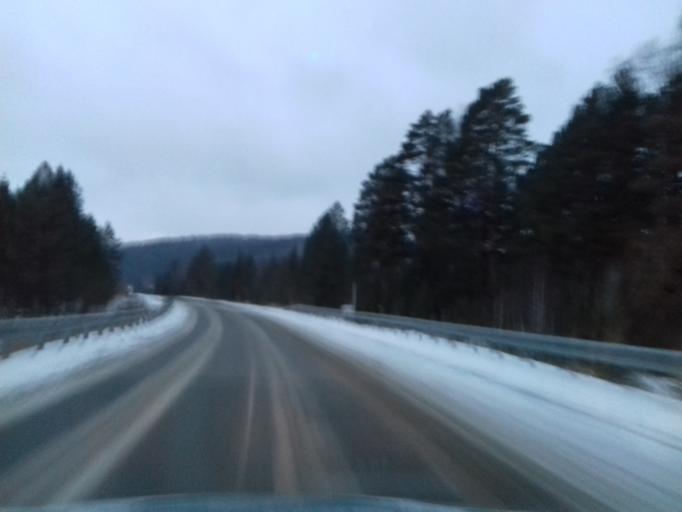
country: RU
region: Bashkortostan
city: Lomovka
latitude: 53.8656
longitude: 58.0320
